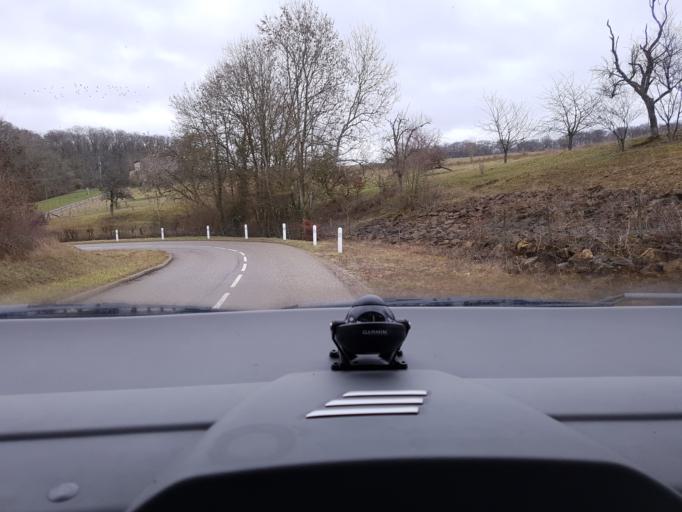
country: FR
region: Lorraine
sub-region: Departement de la Moselle
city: Morhange
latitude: 48.8712
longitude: 6.6674
